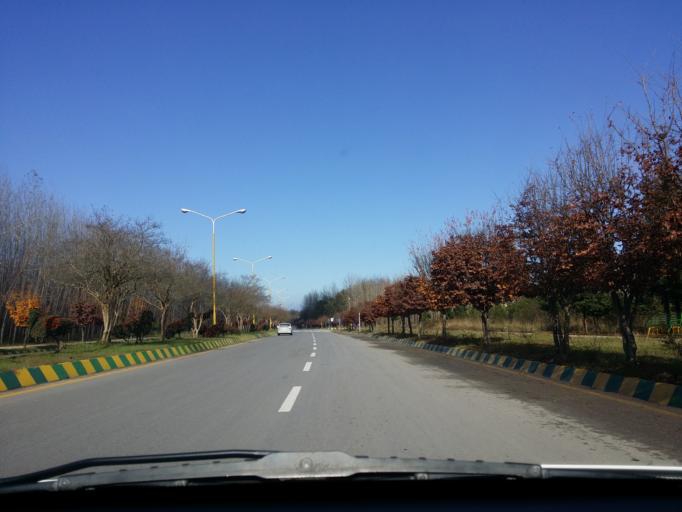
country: IR
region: Mazandaran
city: Chalus
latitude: 36.6768
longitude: 51.3068
